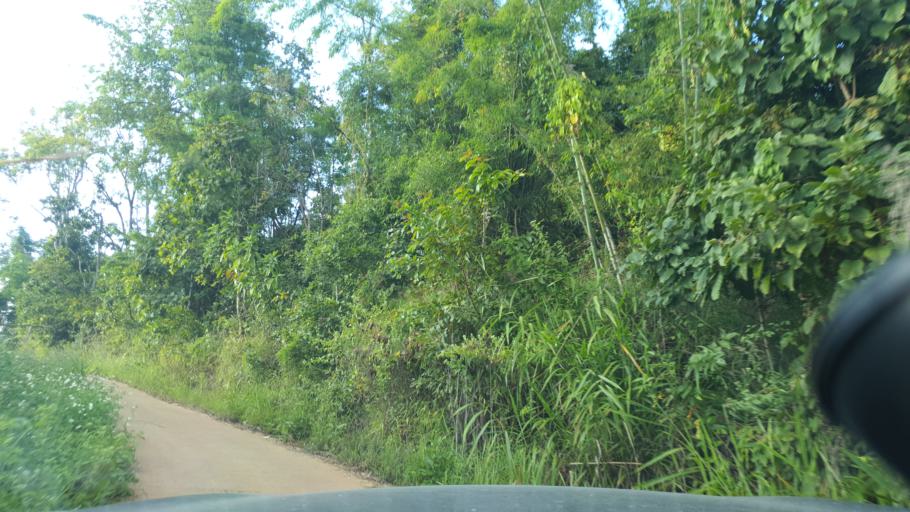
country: TH
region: Chiang Mai
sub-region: Amphoe Chiang Dao
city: Chiang Dao
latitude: 19.4075
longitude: 98.8334
